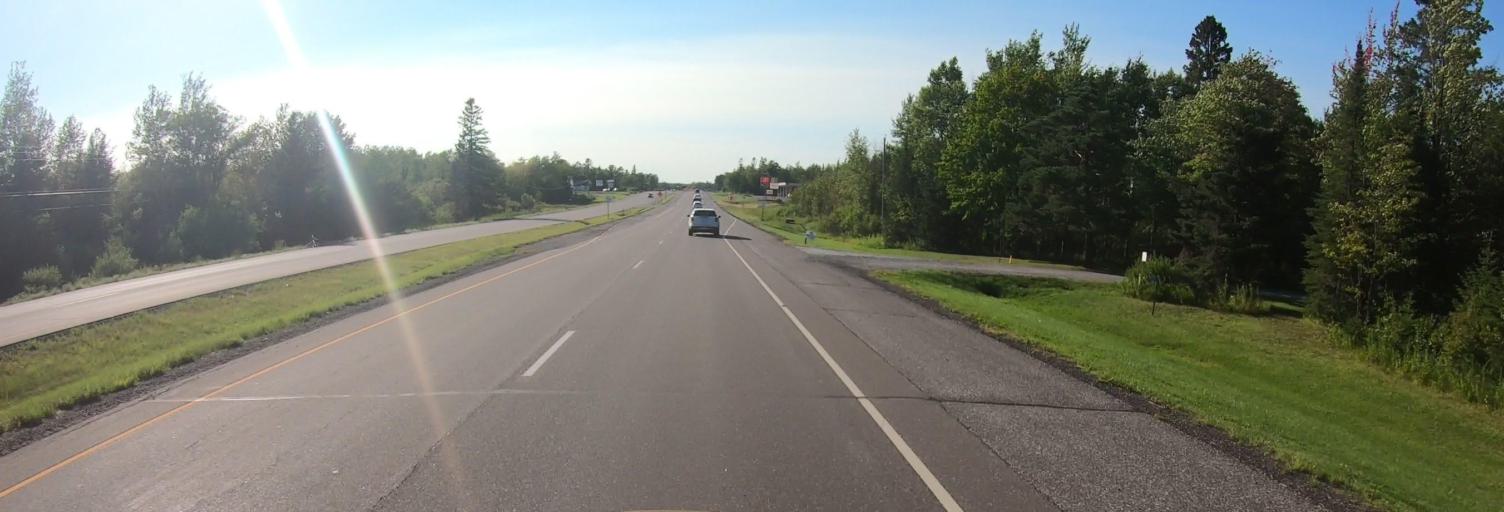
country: US
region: Minnesota
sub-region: Saint Louis County
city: Hermantown
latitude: 46.8470
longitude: -92.2676
